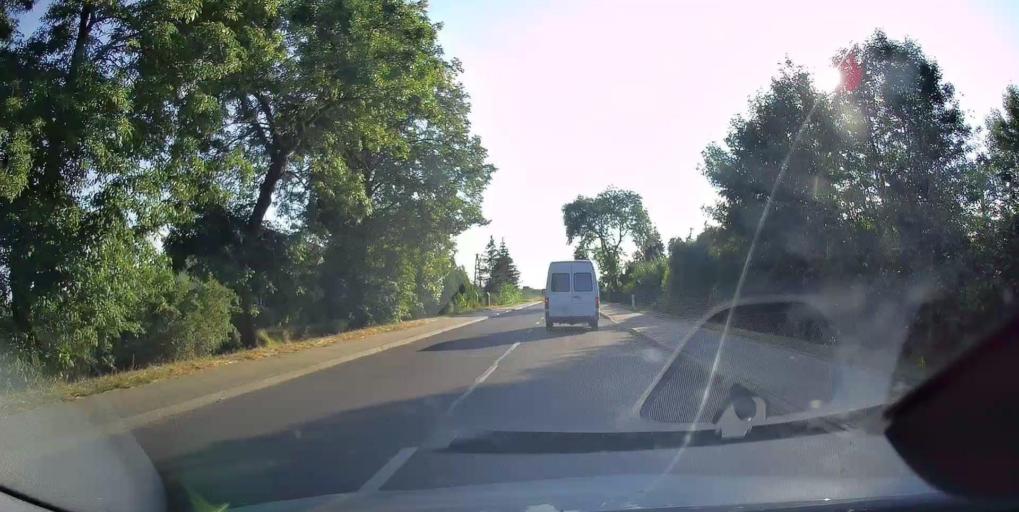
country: PL
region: Lodz Voivodeship
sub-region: Powiat rawski
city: Biala Rawska
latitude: 51.8047
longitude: 20.5548
